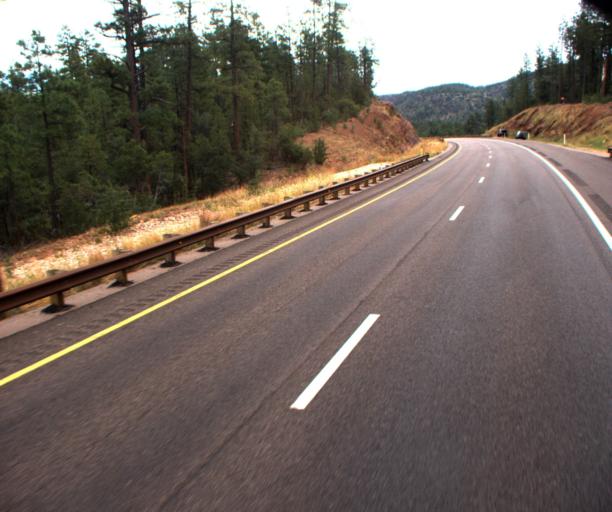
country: US
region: Arizona
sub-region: Gila County
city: Star Valley
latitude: 34.3143
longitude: -111.0568
